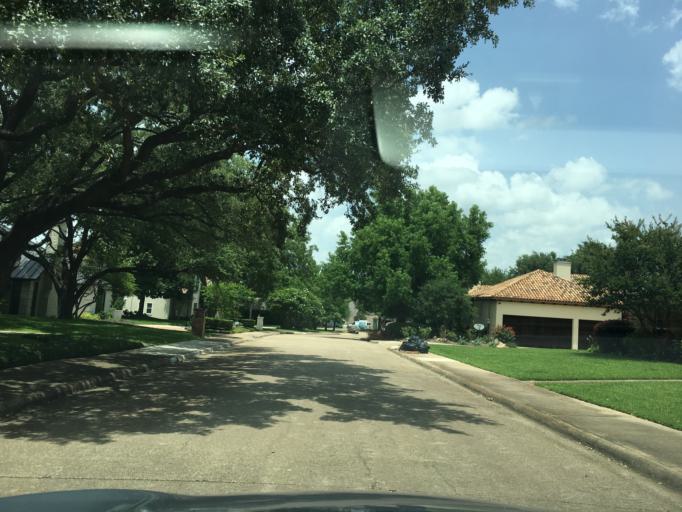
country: US
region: Texas
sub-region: Dallas County
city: University Park
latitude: 32.9069
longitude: -96.7956
